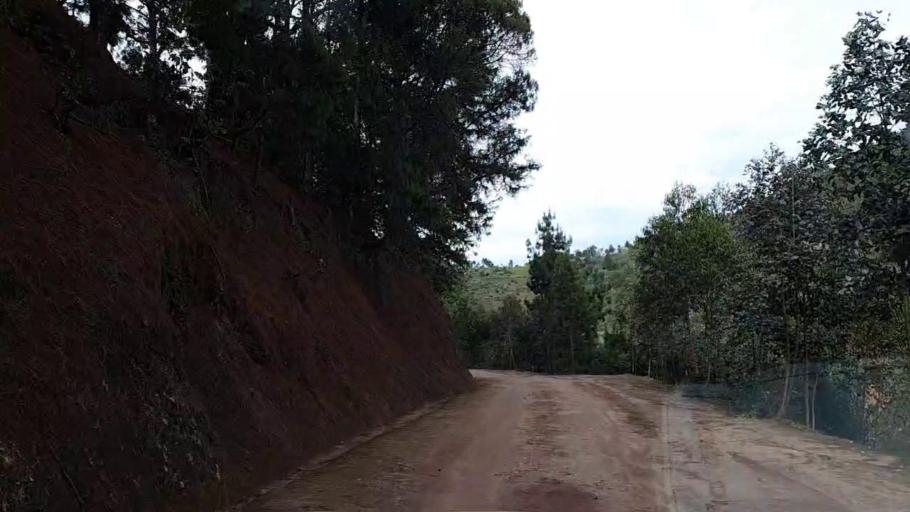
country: RW
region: Southern Province
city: Nzega
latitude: -2.4110
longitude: 29.4552
